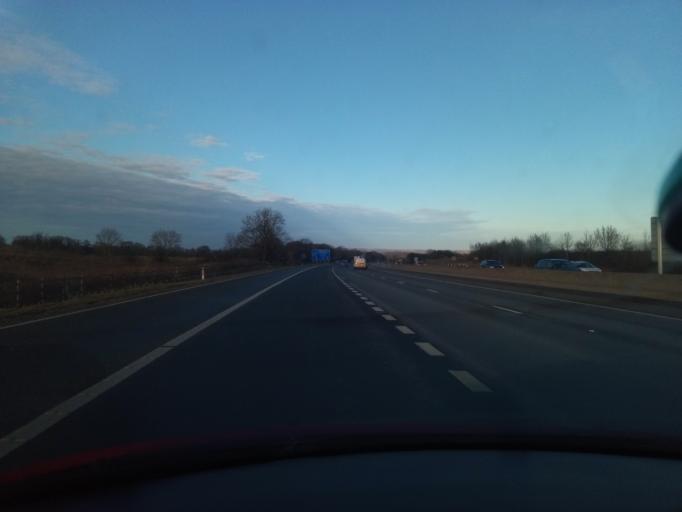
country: GB
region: England
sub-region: Darlington
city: High Coniscliffe
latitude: 54.4608
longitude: -1.6690
